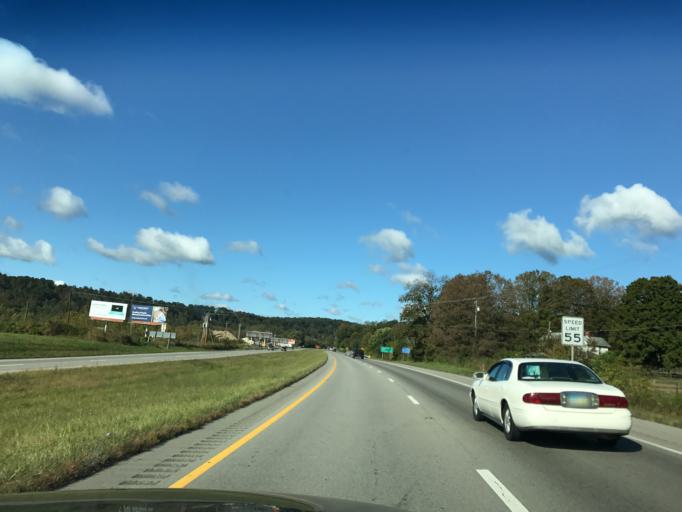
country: US
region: Ohio
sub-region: Athens County
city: Chauncey
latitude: 39.3902
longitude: -82.1467
